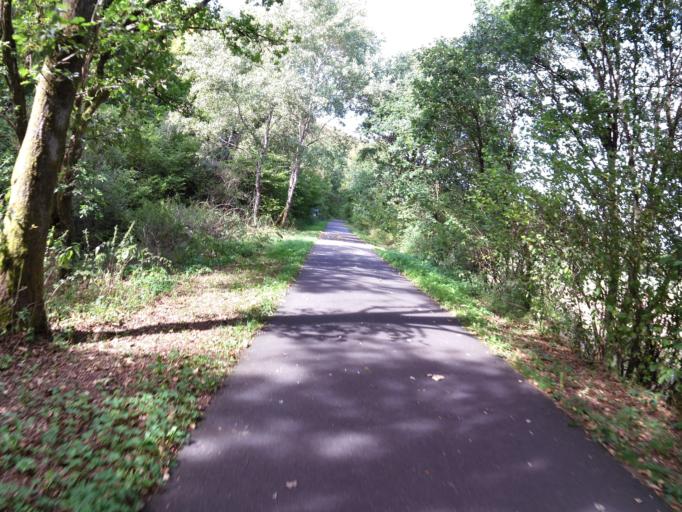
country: DE
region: Rheinland-Pfalz
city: Pronsfeld
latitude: 50.1526
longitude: 6.3352
